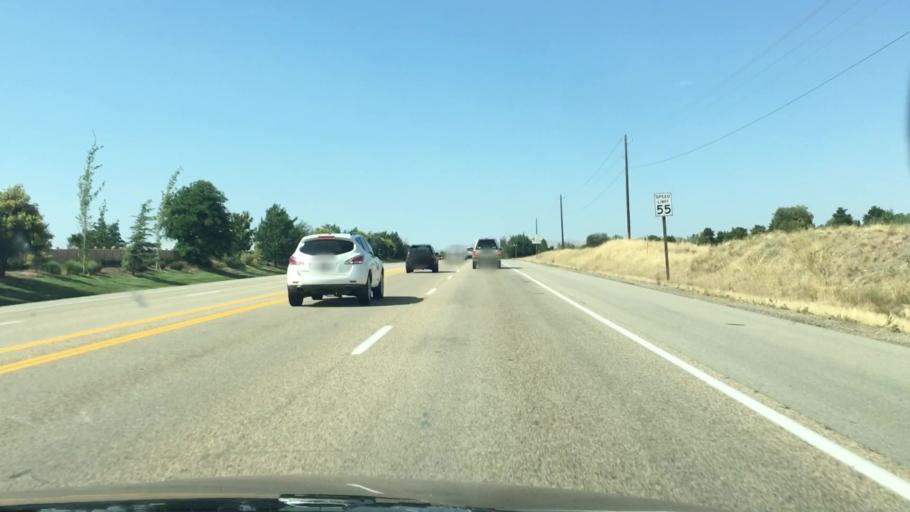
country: US
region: Idaho
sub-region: Ada County
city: Eagle
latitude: 43.6966
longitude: -116.3190
